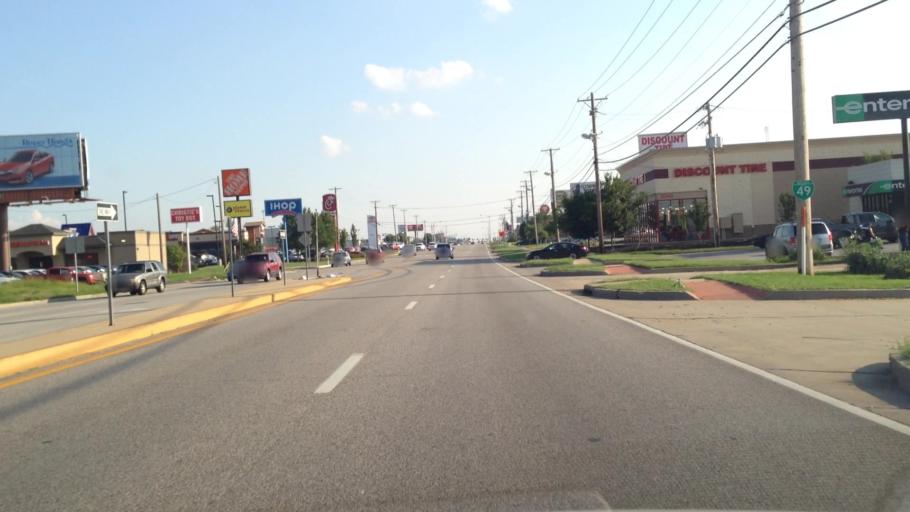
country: US
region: Missouri
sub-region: Jasper County
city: Duquesne
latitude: 37.0686
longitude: -94.4780
